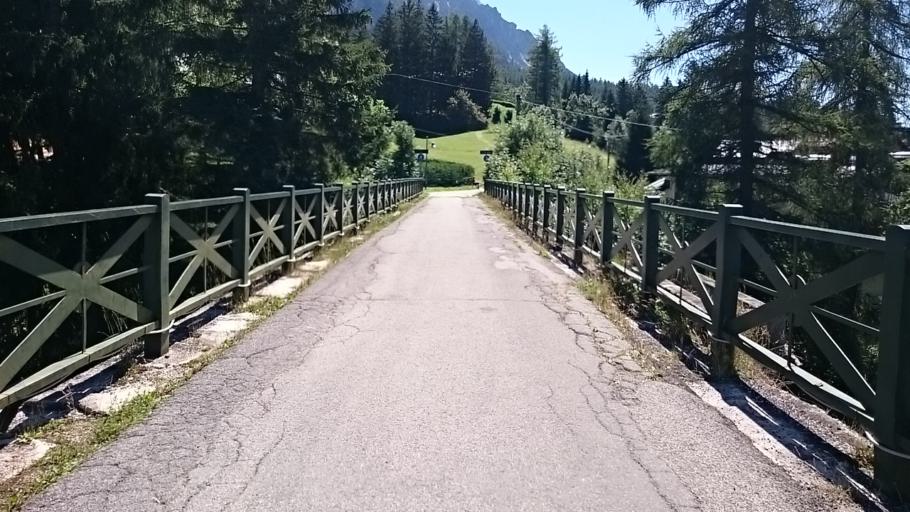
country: IT
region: Veneto
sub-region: Provincia di Belluno
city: Cortina d'Ampezzo
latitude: 46.5375
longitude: 12.1413
